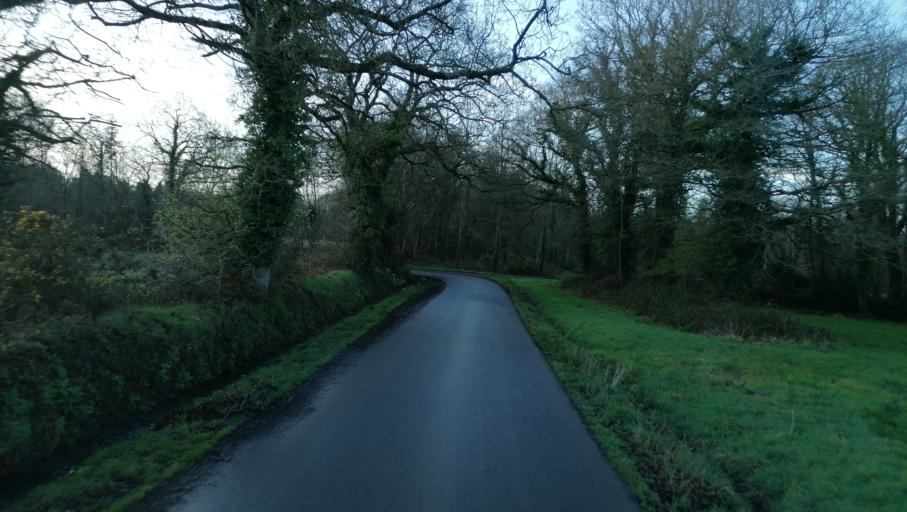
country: FR
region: Brittany
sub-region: Departement des Cotes-d'Armor
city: Pleguien
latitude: 48.6587
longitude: -2.9464
